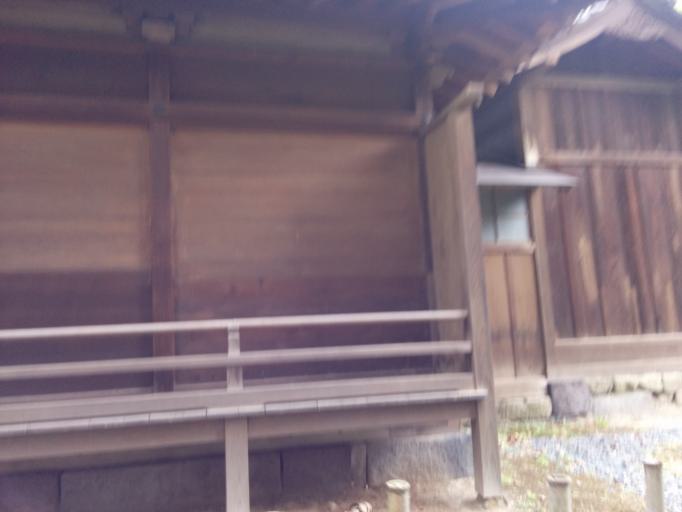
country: JP
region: Tokyo
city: Tokyo
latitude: 35.6611
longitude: 139.7655
